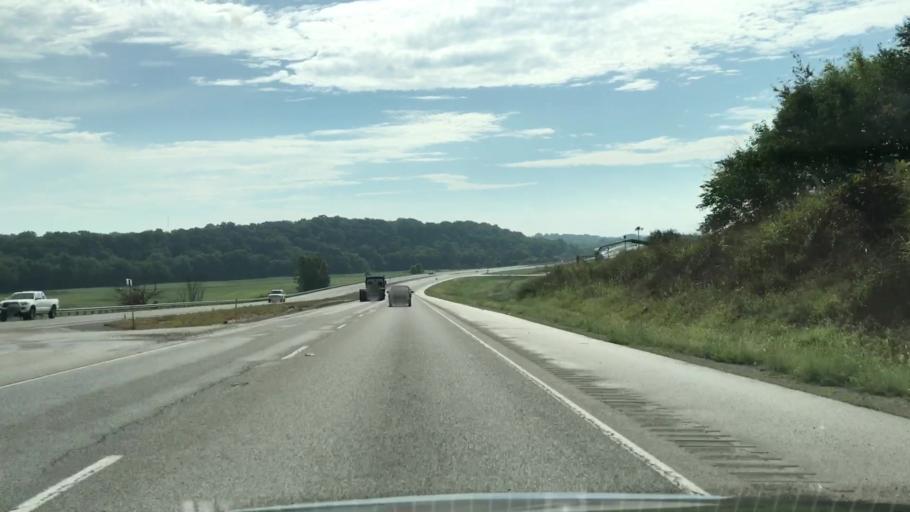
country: US
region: Kentucky
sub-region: Warren County
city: Plano
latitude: 36.9010
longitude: -86.3906
